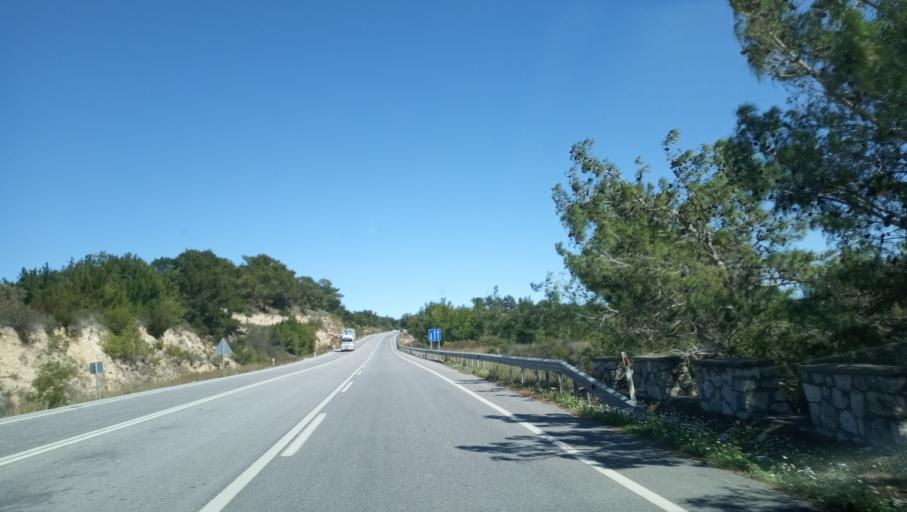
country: TR
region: Antalya
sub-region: Manavgat
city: Kizilagac
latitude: 36.7531
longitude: 31.6250
